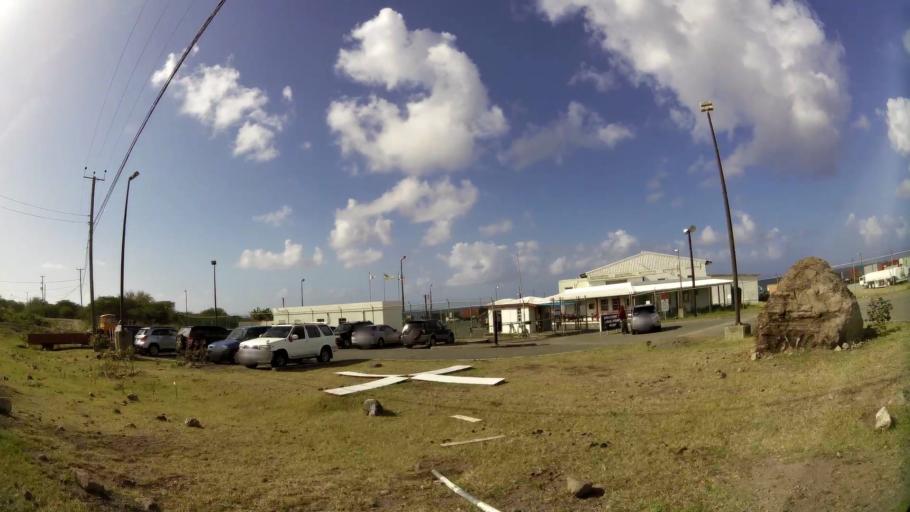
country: KN
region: Saint John Figtree
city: Fig Tree
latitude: 17.1108
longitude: -62.6209
